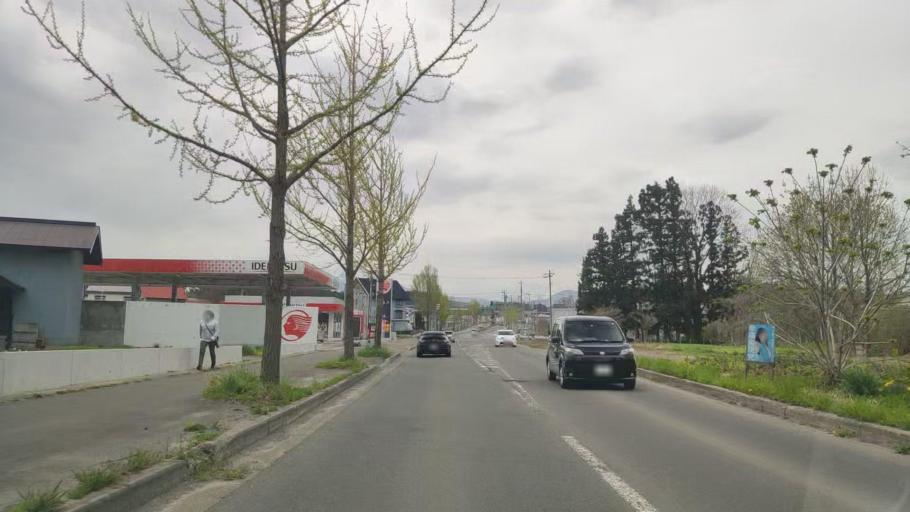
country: JP
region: Aomori
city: Aomori Shi
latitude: 40.7933
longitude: 140.7859
